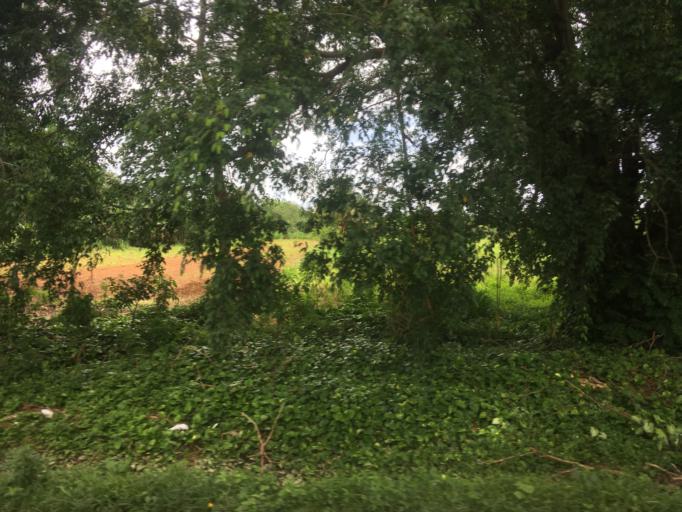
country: CU
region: Matanzas
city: Colon
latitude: 22.7103
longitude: -80.8909
